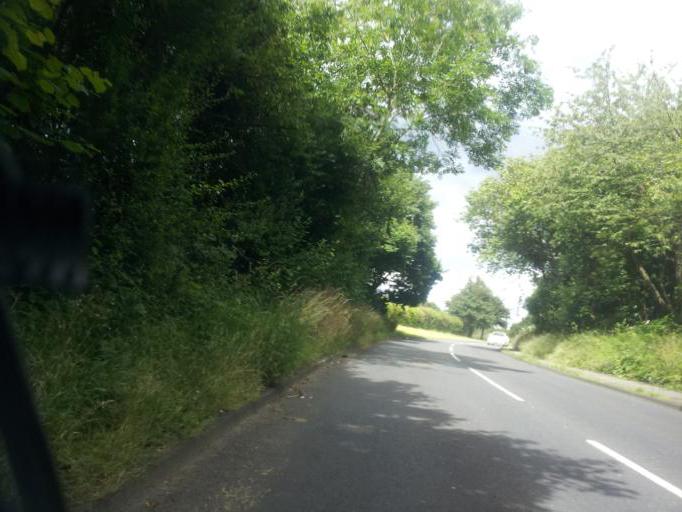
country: GB
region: England
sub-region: Kent
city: Wateringbury
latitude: 51.2576
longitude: 0.4272
